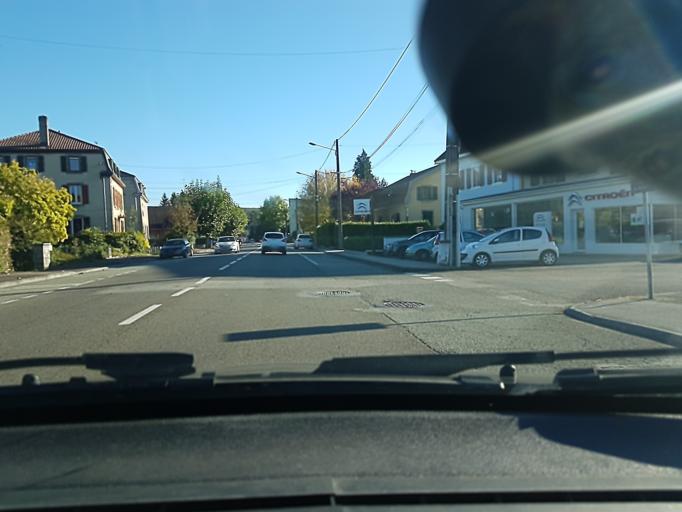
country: FR
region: Franche-Comte
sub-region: Departement du Doubs
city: Seloncourt
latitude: 47.4679
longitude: 6.8540
